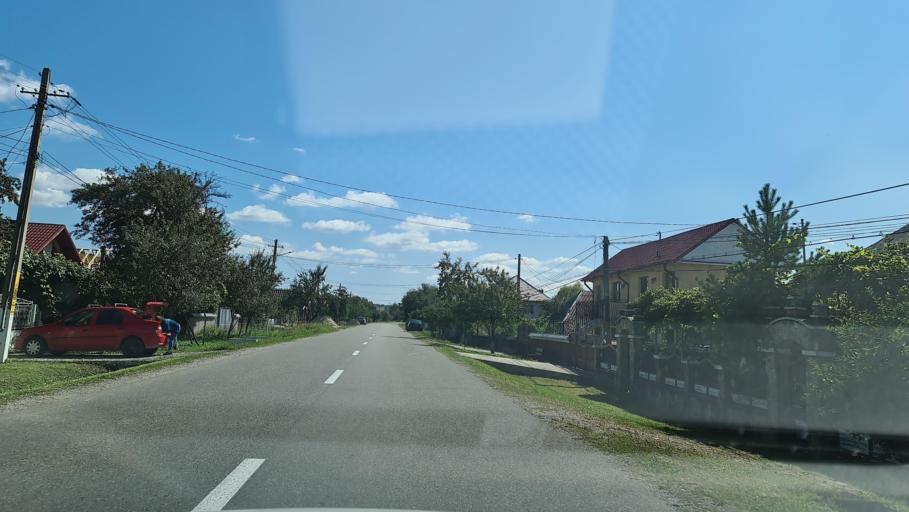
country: RO
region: Bacau
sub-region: Comuna Balcani
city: Balcani
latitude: 46.6502
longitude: 26.5603
